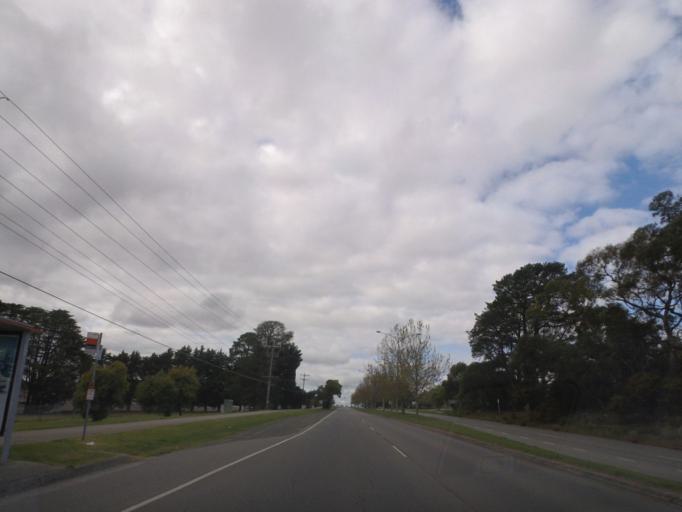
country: AU
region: Victoria
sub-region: Knox
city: Wantirna
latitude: -37.8515
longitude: 145.2230
